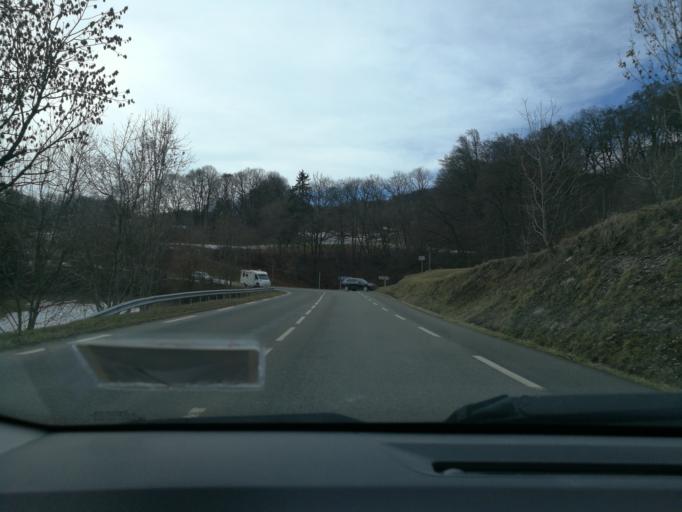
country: FR
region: Rhone-Alpes
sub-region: Departement de la Haute-Savoie
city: Sallanches
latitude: 45.9262
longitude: 6.6328
